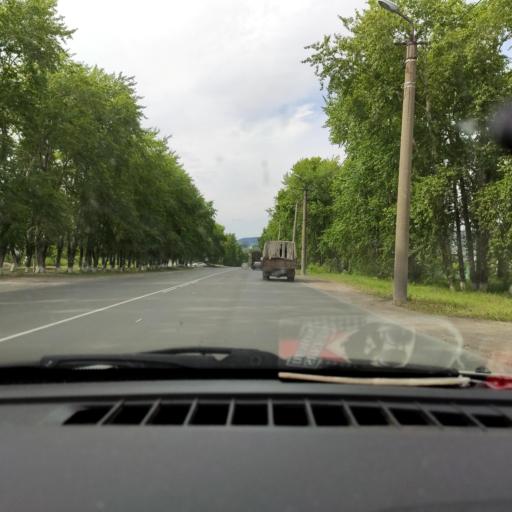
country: RU
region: Perm
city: Chusovoy
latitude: 58.2758
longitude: 57.8151
